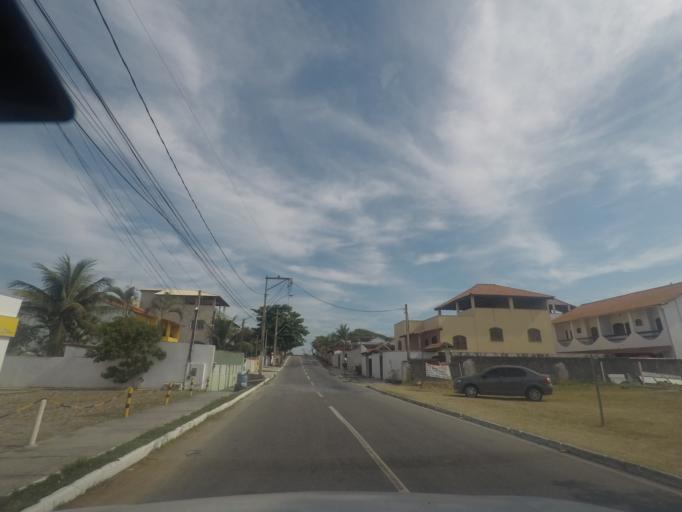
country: BR
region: Rio de Janeiro
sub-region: Marica
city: Marica
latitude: -22.9593
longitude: -42.8148
